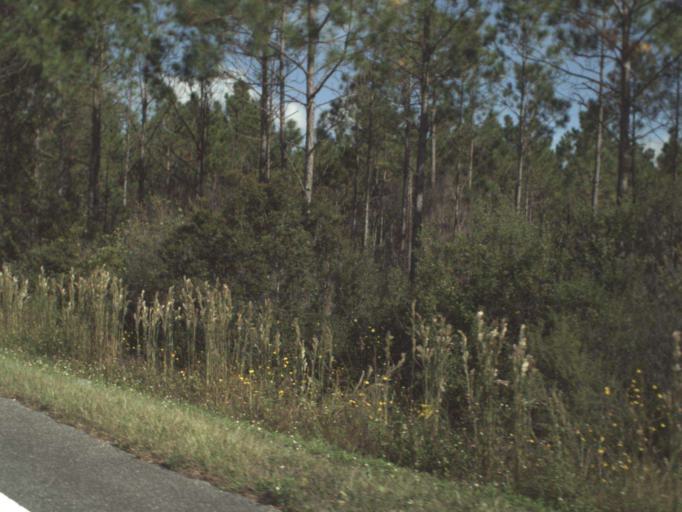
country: US
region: Florida
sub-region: Franklin County
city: Eastpoint
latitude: 29.8006
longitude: -84.8320
